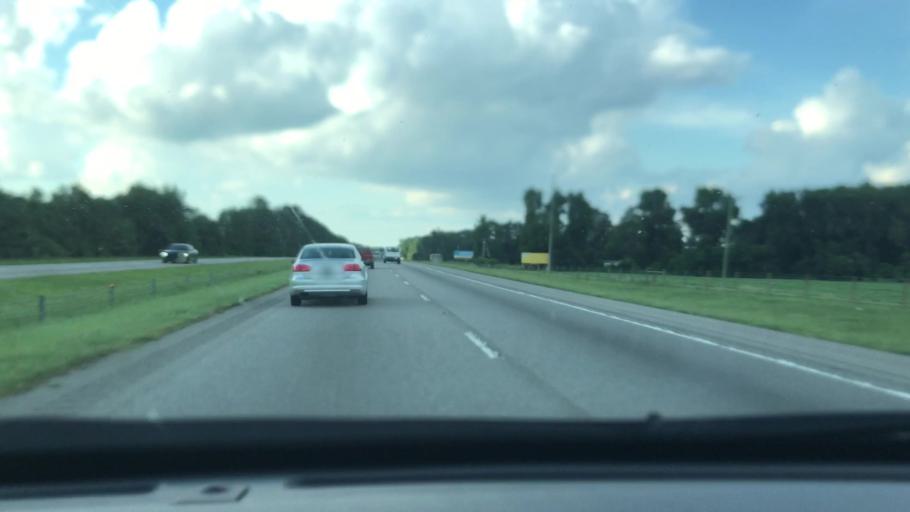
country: US
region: North Carolina
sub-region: Cumberland County
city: Hope Mills
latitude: 34.8920
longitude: -78.9597
